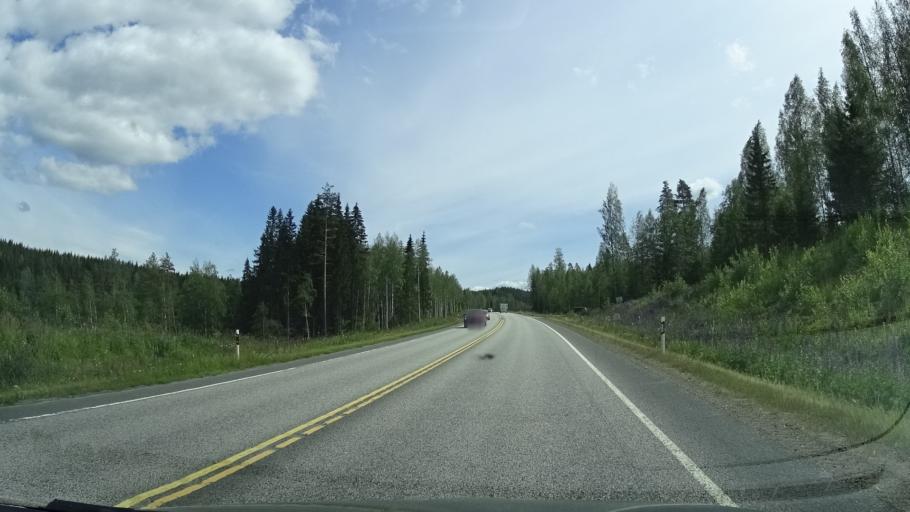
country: FI
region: Central Finland
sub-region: Jyvaeskylae
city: Jyvaeskylae
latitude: 62.2537
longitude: 25.6306
